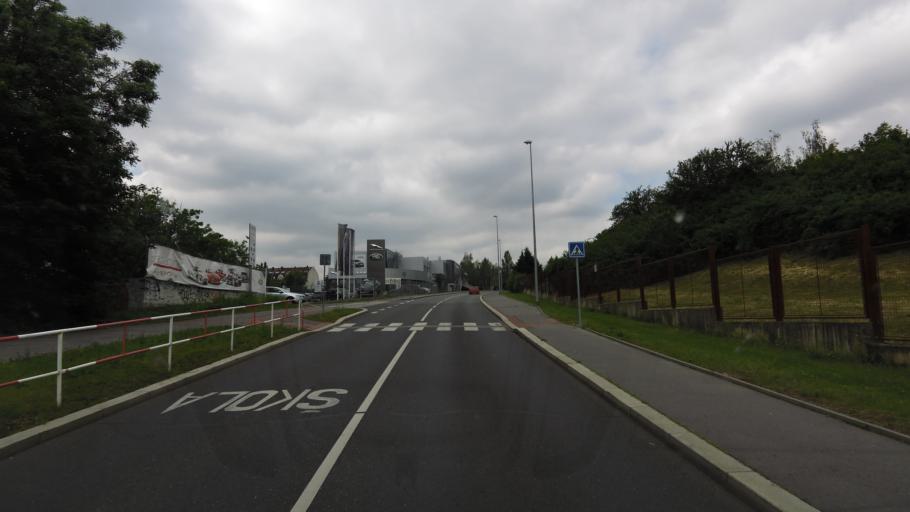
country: CZ
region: Praha
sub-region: Praha 1
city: Mala Strana
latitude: 50.0735
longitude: 14.3552
